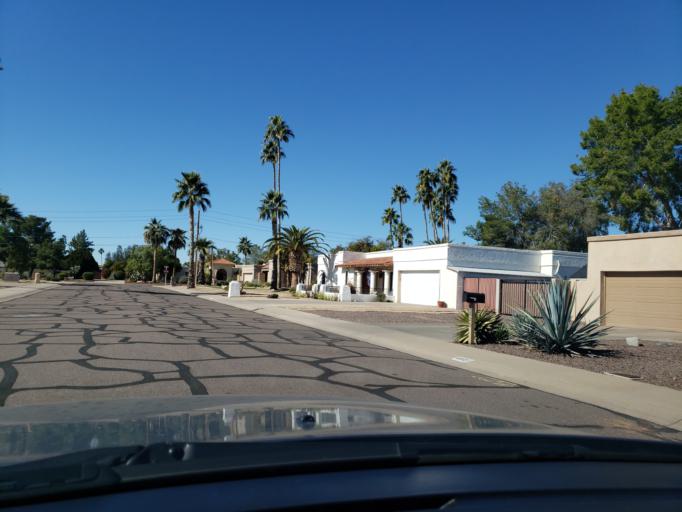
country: US
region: Arizona
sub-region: Maricopa County
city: Paradise Valley
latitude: 33.6135
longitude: -111.9335
